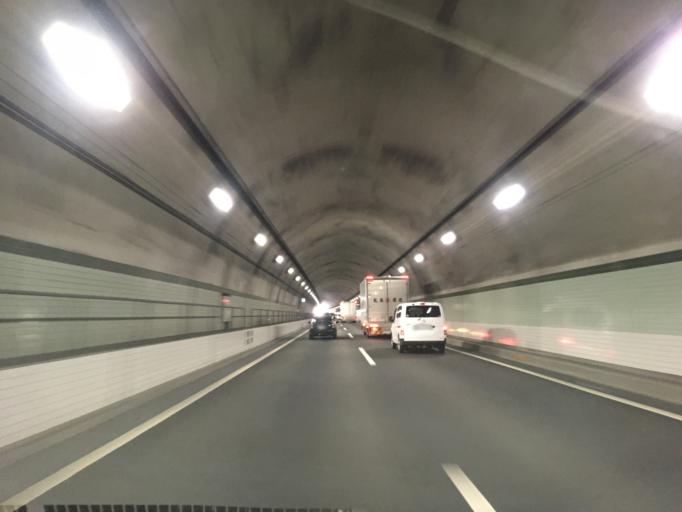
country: JP
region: Tokyo
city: Itsukaichi
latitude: 35.6721
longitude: 139.2509
